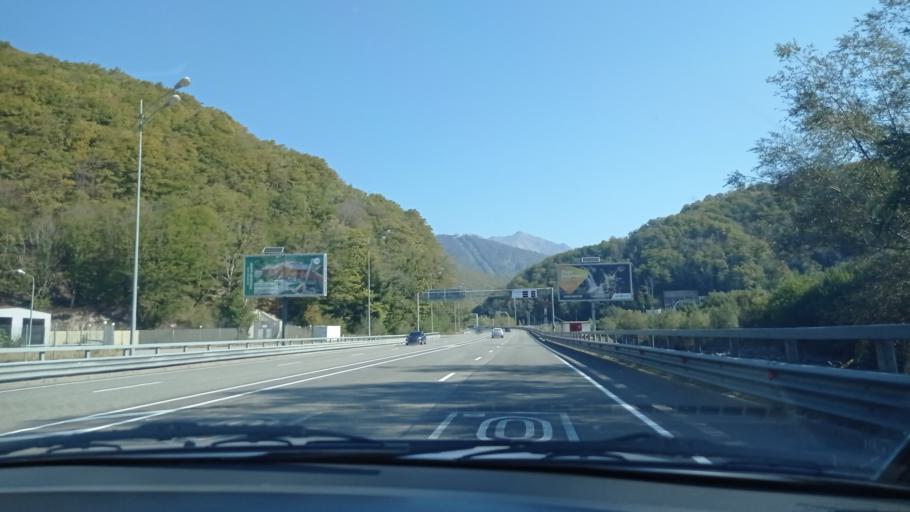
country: RU
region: Krasnodarskiy
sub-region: Sochi City
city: Krasnaya Polyana
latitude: 43.6851
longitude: 40.2391
